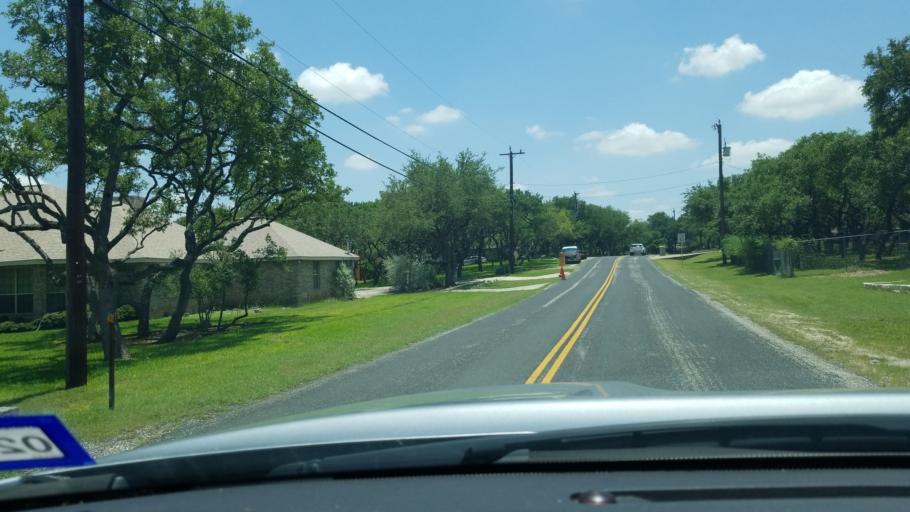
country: US
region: Texas
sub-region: Bexar County
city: Timberwood Park
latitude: 29.7018
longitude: -98.5074
